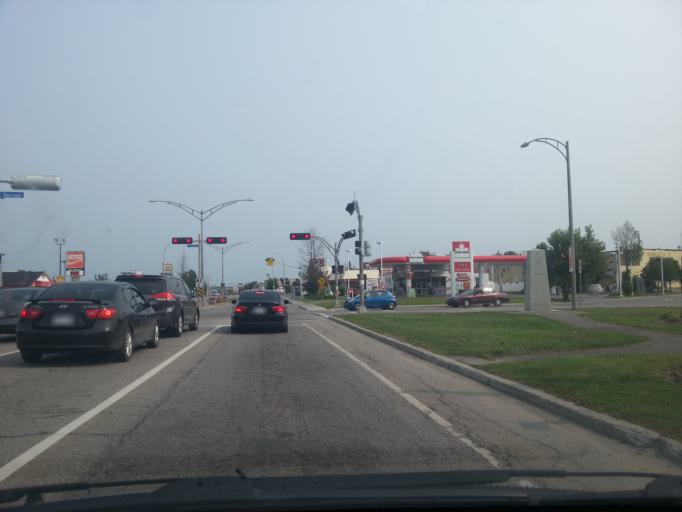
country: CA
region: Quebec
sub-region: Outaouais
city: Gatineau
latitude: 45.4609
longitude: -75.6997
